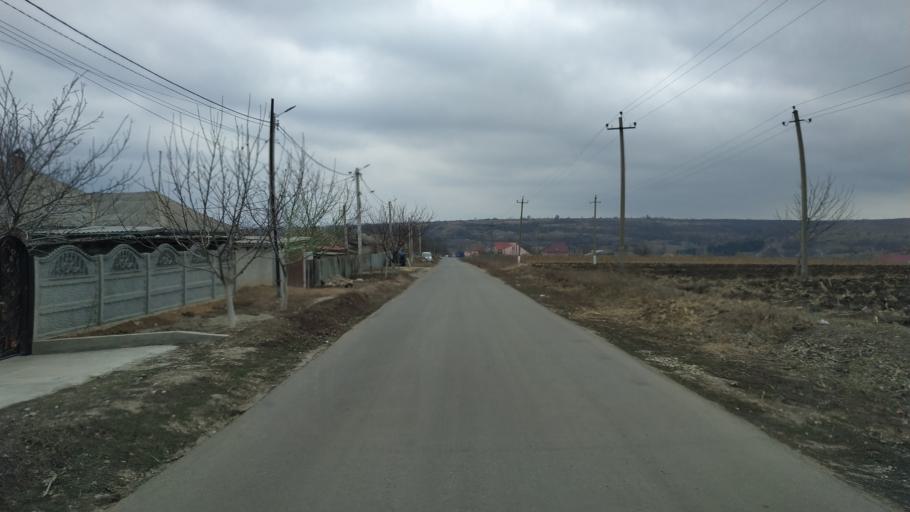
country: MD
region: Laloveni
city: Ialoveni
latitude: 46.9306
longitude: 28.7738
